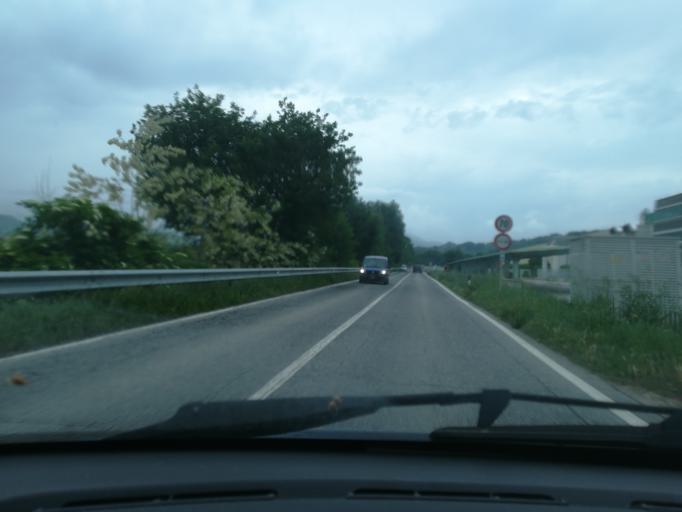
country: IT
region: The Marches
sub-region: Provincia di Macerata
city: San Severino Marche
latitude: 43.2605
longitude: 13.2389
